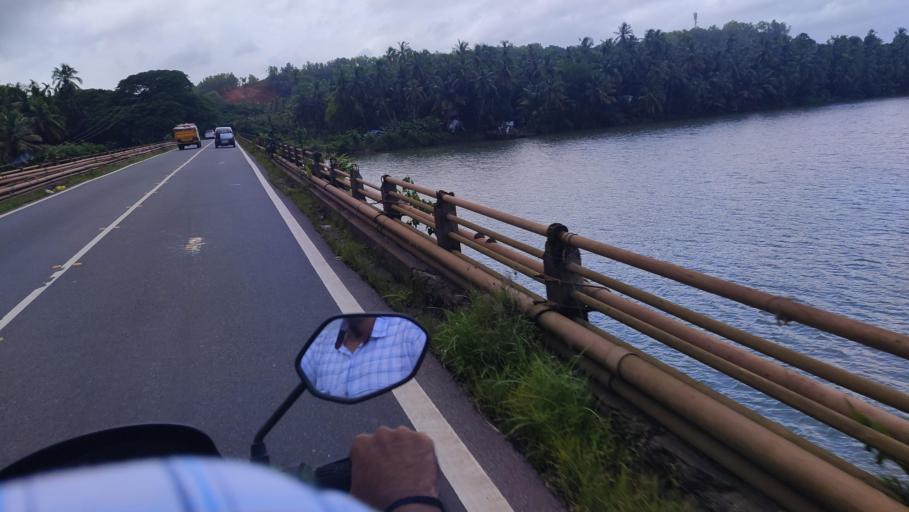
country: IN
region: Kerala
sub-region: Kasaragod District
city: Nileshwar
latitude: 12.2372
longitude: 75.1505
